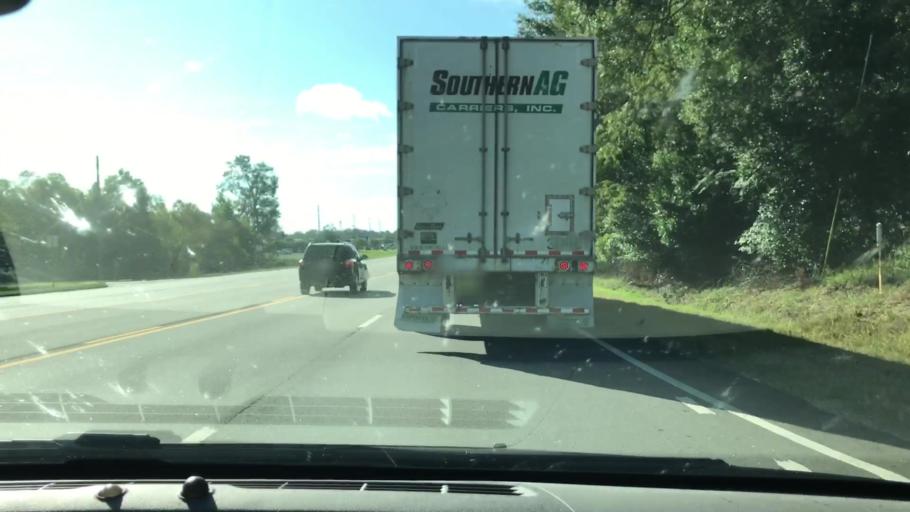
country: US
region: Georgia
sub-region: Dougherty County
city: Albany
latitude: 31.6343
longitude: -84.2447
